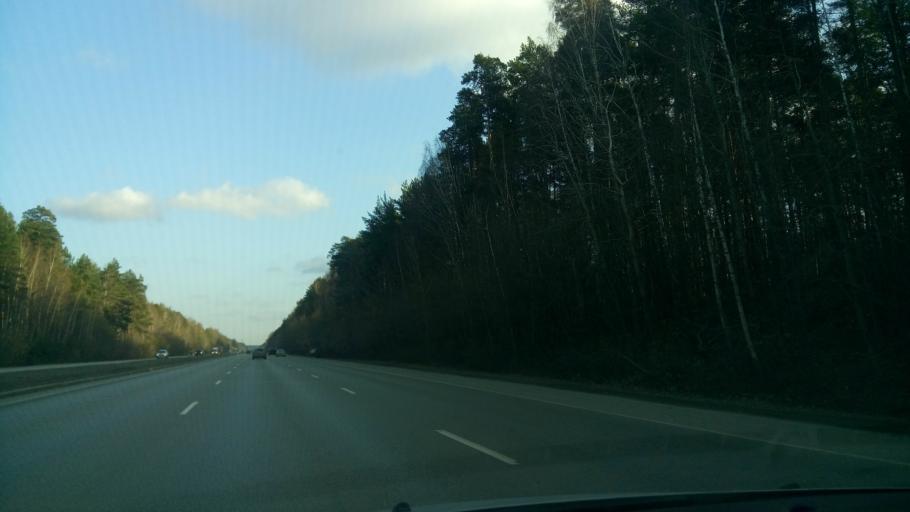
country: RU
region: Sverdlovsk
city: Istok
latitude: 56.8151
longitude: 60.7399
